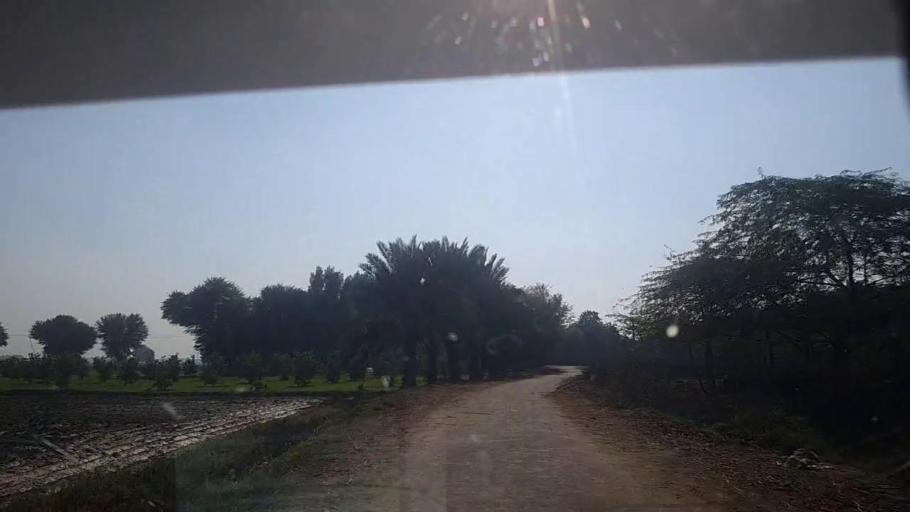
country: PK
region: Sindh
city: Gambat
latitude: 27.3884
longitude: 68.5994
